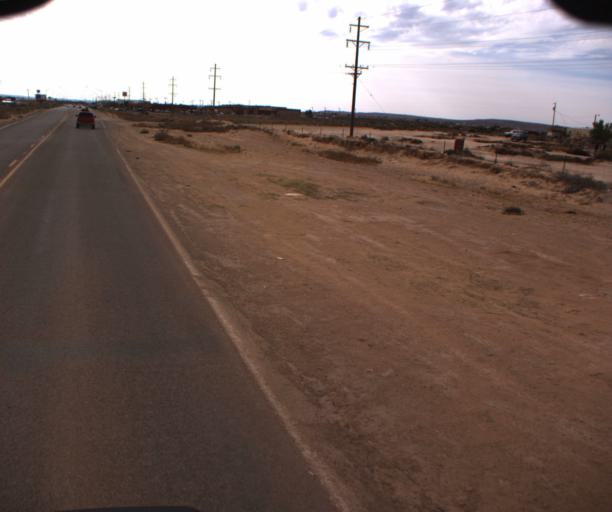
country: US
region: Arizona
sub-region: Apache County
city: Chinle
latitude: 36.1681
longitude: -109.5860
